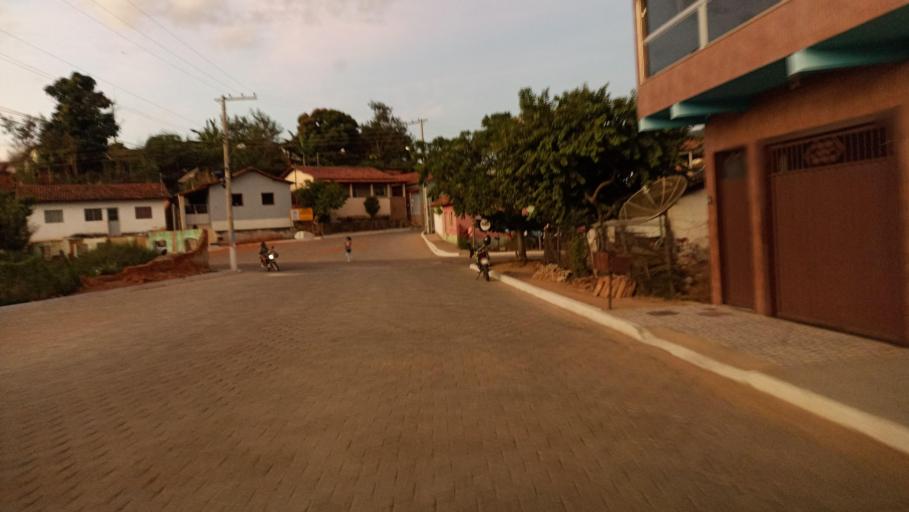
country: BR
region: Minas Gerais
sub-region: Aracuai
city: Aracuai
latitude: -16.6181
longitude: -42.1852
